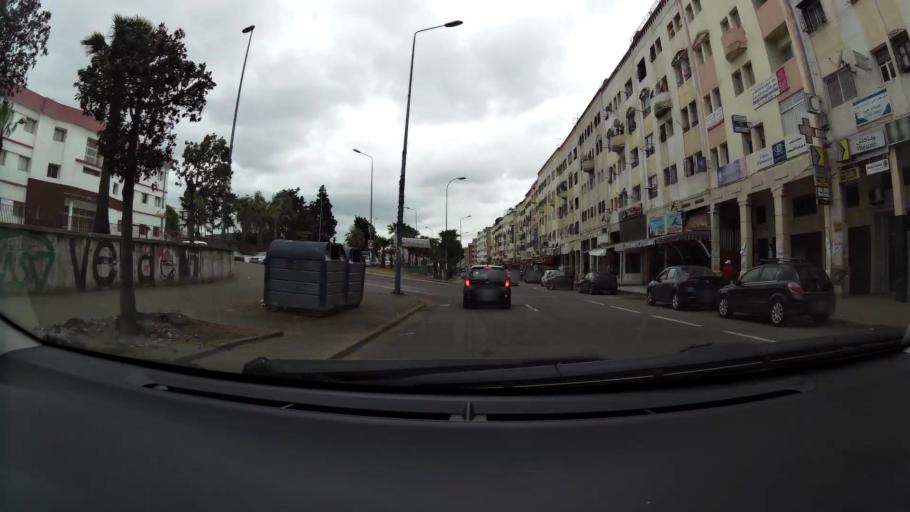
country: MA
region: Grand Casablanca
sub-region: Mediouna
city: Tit Mellil
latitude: 33.5670
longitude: -7.5415
